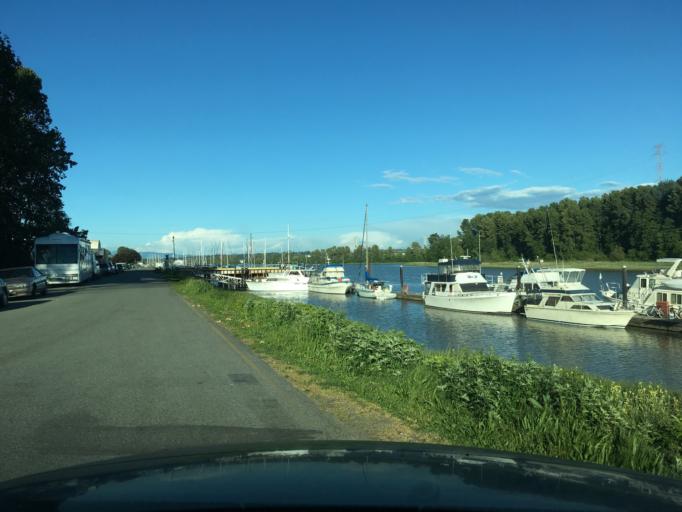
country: CA
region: British Columbia
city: Delta
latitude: 49.1624
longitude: -122.9940
